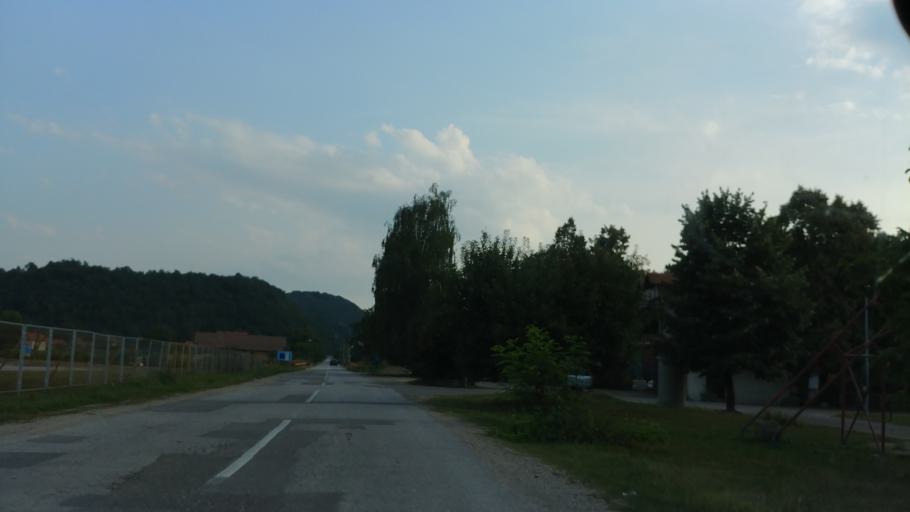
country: BA
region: Republika Srpska
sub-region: Opstina Ugljevik
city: Ugljevik
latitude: 44.6948
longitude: 19.0137
